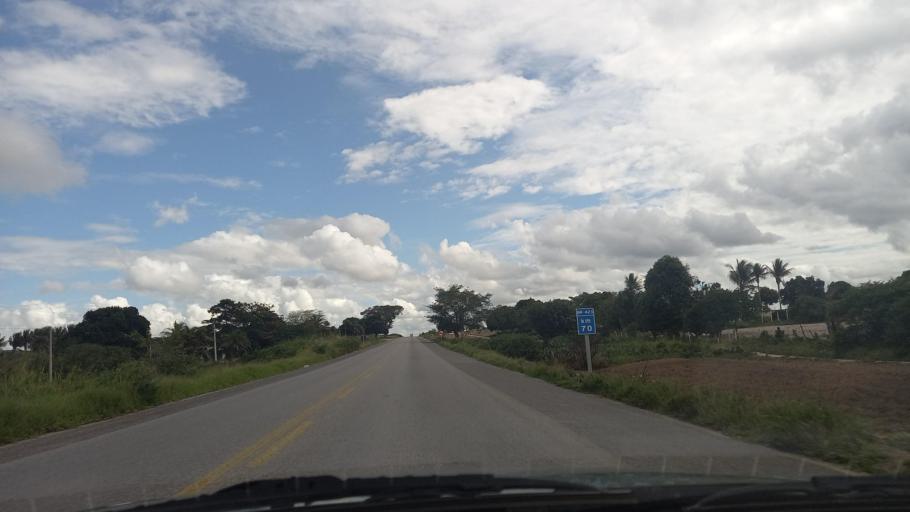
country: BR
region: Pernambuco
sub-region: Lajedo
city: Lajedo
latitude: -8.6799
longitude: -36.4047
